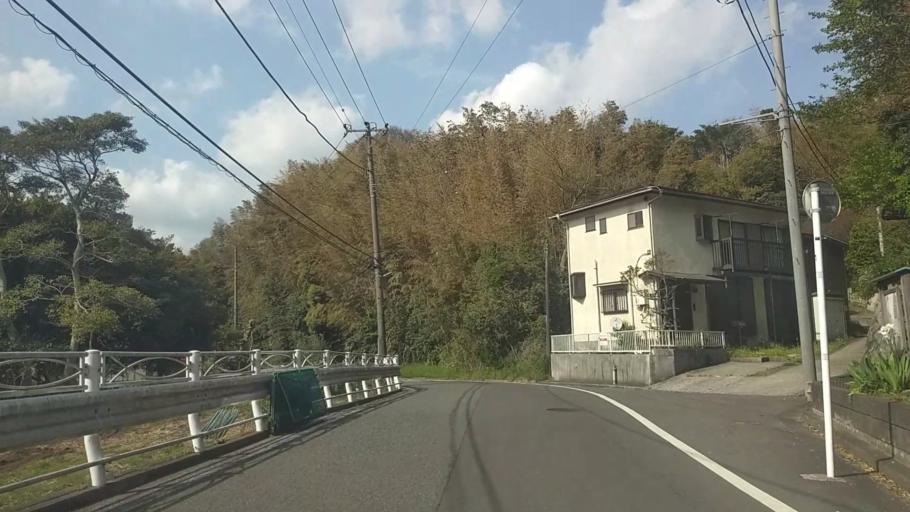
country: JP
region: Kanagawa
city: Kamakura
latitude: 35.3844
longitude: 139.5655
